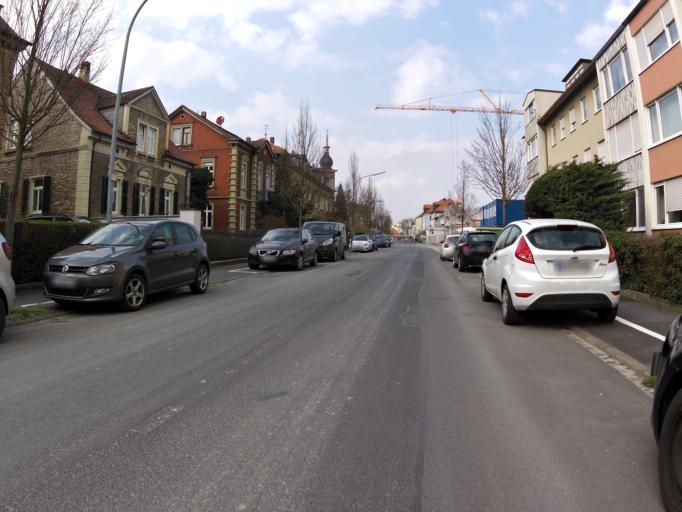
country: DE
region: Bavaria
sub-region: Regierungsbezirk Unterfranken
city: Kitzingen
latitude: 49.7328
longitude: 10.1629
